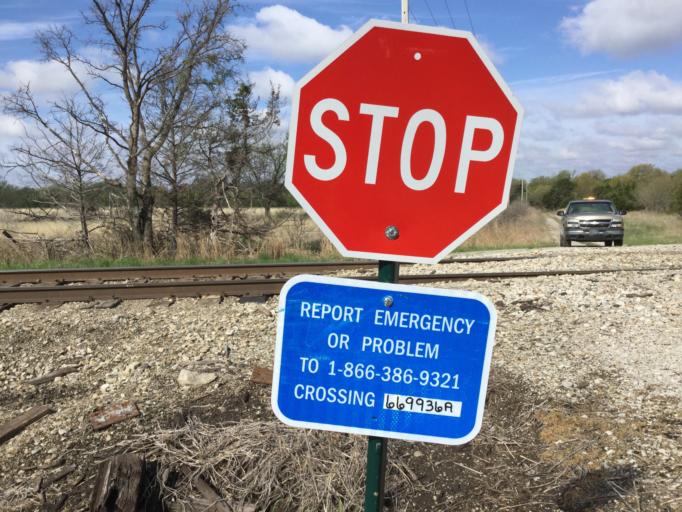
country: US
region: Kansas
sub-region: Wilson County
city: Fredonia
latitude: 37.5044
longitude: -95.8211
